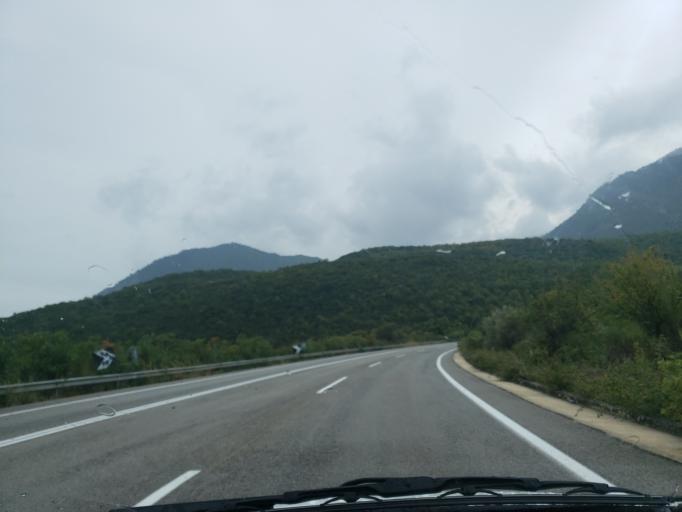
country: GR
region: Central Greece
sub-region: Nomos Fthiotidos
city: Anthili
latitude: 38.7910
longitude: 22.4932
